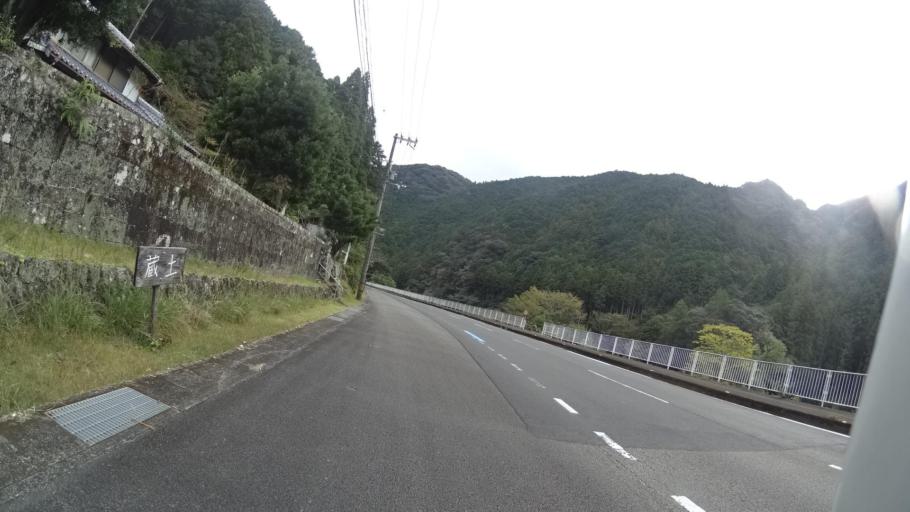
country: JP
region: Wakayama
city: Shingu
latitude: 33.5511
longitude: 135.7069
